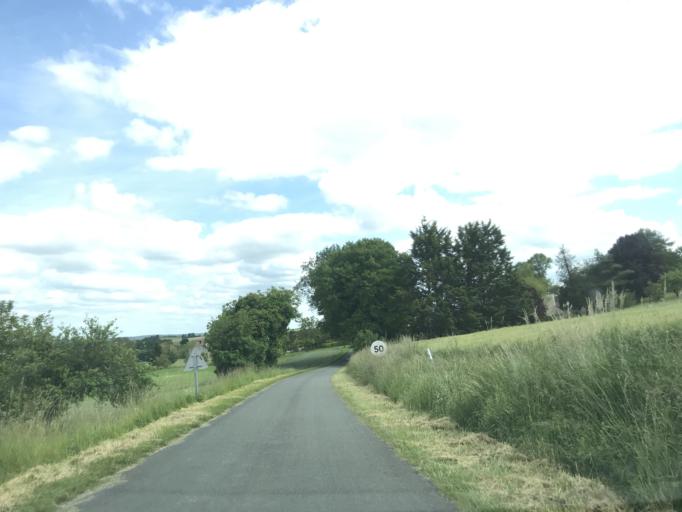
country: FR
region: Aquitaine
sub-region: Departement de la Dordogne
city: Saint-Aulaye
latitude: 45.2714
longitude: 0.1174
